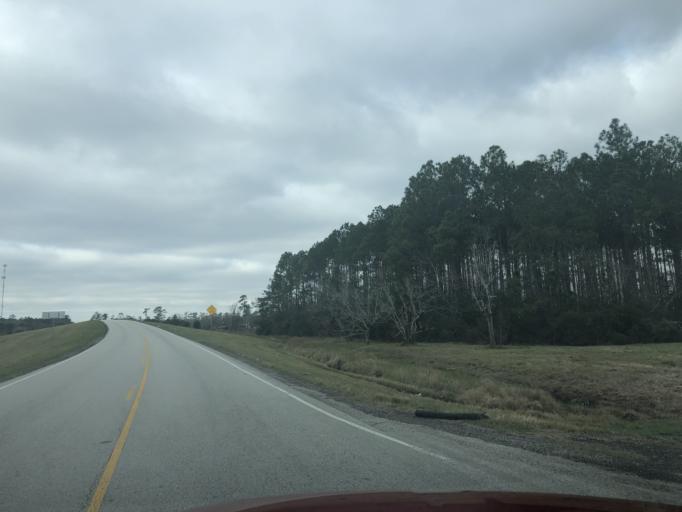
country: US
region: Texas
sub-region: Jefferson County
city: Fannett
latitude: 29.9314
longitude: -94.2655
